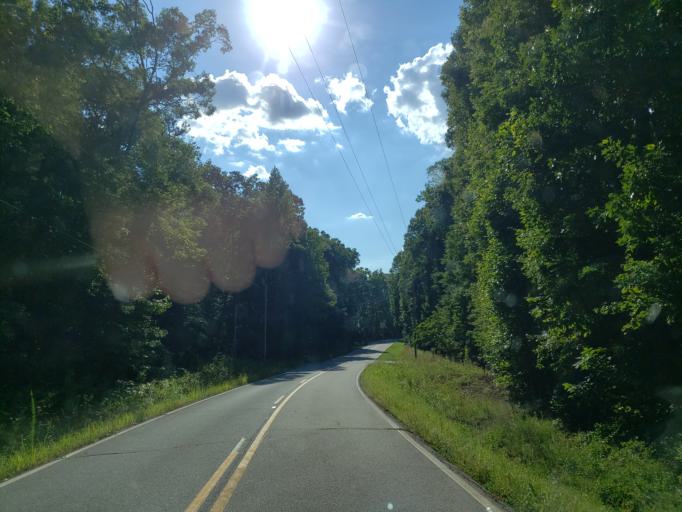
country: US
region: Georgia
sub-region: Carroll County
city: Carrollton
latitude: 33.6501
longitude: -85.0968
